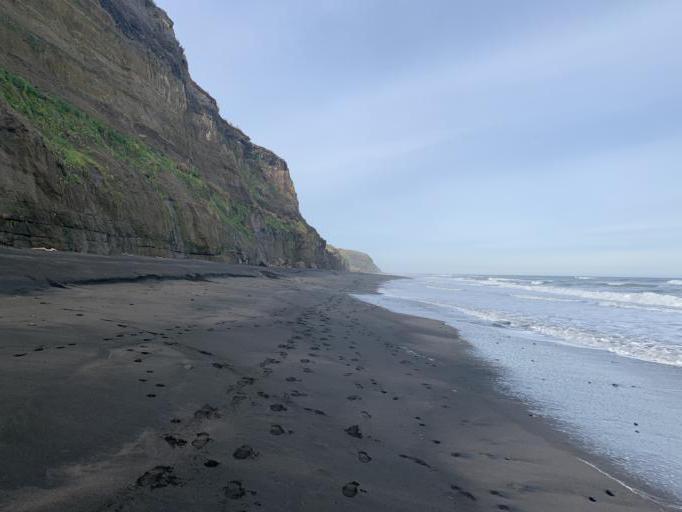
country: NZ
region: Taranaki
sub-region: South Taranaki District
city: Opunake
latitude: -39.5639
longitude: 174.0541
